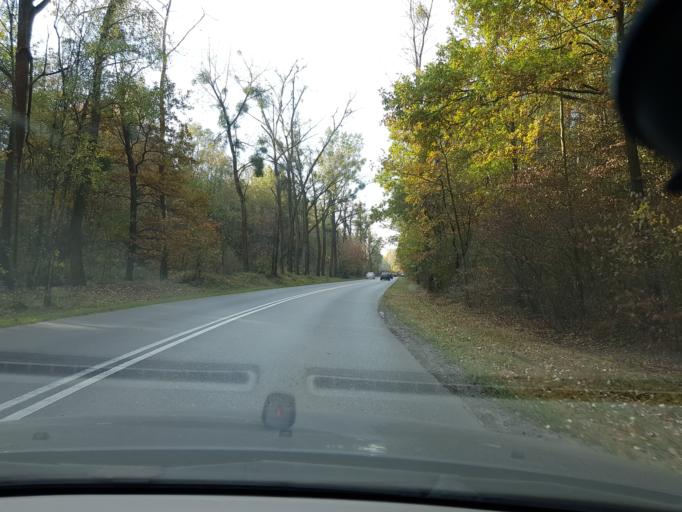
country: PL
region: Masovian Voivodeship
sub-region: Powiat warszawski zachodni
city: Babice
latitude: 52.2732
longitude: 20.8751
